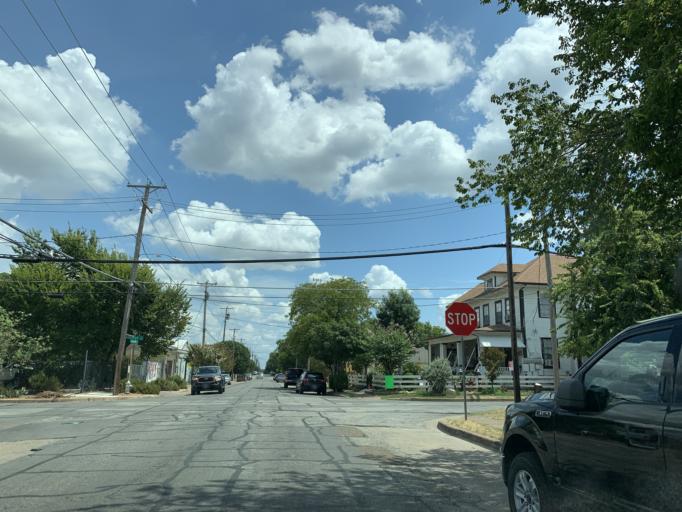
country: US
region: Texas
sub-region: Dallas County
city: Dallas
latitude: 32.7490
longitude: -96.8360
